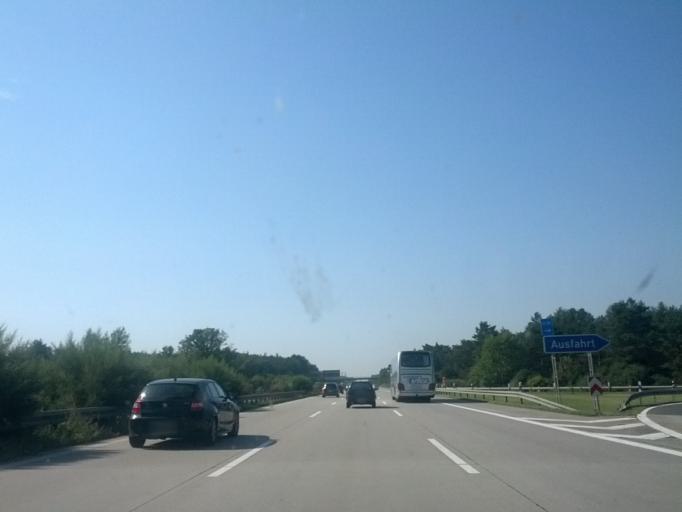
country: DE
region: Brandenburg
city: Linthe
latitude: 52.1577
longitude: 12.7808
